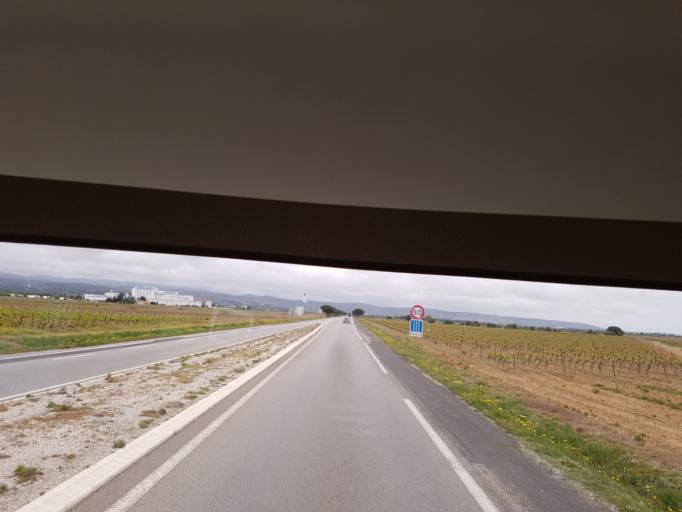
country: FR
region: Languedoc-Roussillon
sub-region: Departement des Pyrenees-Orientales
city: Salses-le-Chateau
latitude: 42.8005
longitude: 2.9101
